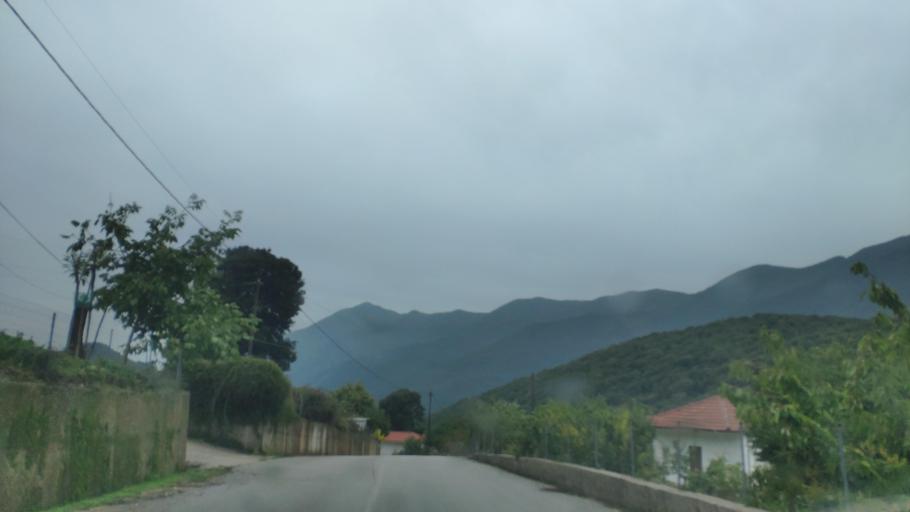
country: GR
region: Epirus
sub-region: Nomos Thesprotias
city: Paramythia
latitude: 39.4163
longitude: 20.6237
